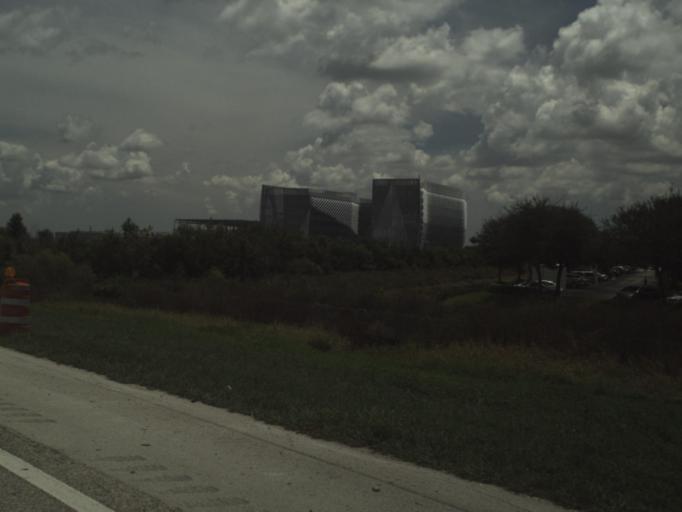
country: US
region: Florida
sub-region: Miami-Dade County
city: Country Club
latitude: 25.9892
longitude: -80.3430
